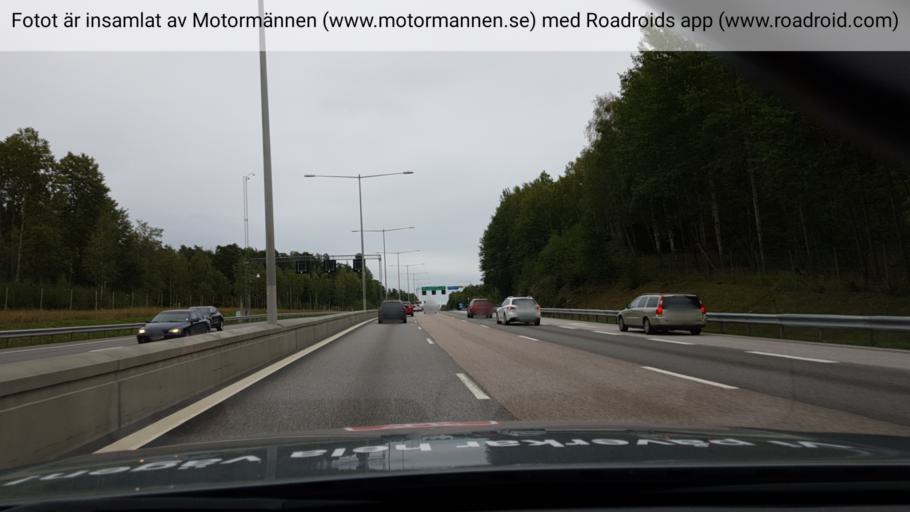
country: SE
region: Stockholm
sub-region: Salems Kommun
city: Ronninge
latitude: 59.2116
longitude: 17.7470
